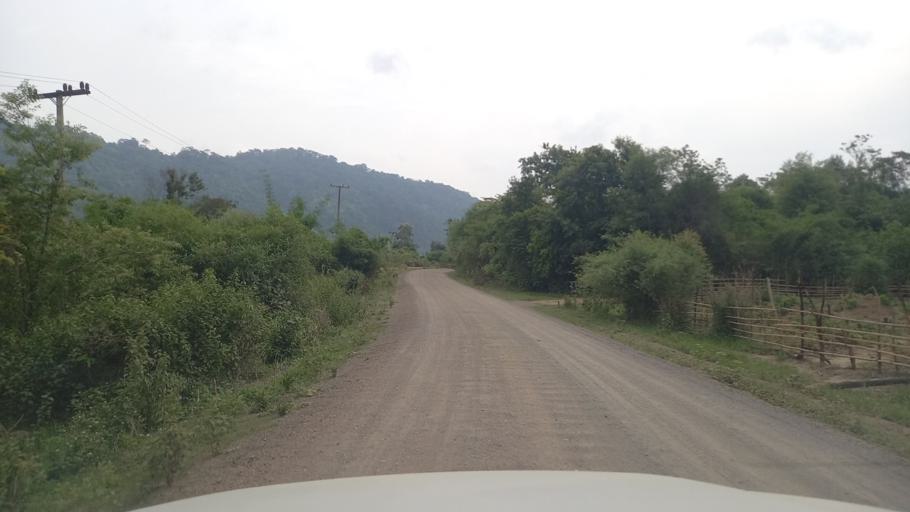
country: LA
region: Bolikhamxai
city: Ban Nahin
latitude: 18.1493
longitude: 104.7366
